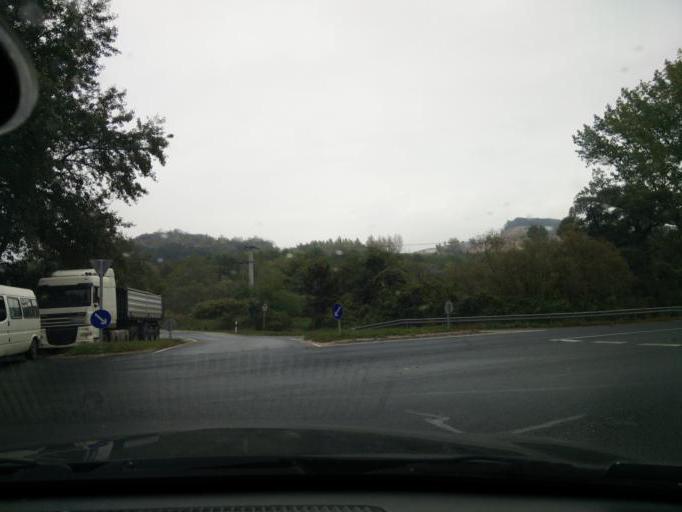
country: HU
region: Komarom-Esztergom
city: Tatabanya
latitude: 47.5636
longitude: 18.4448
